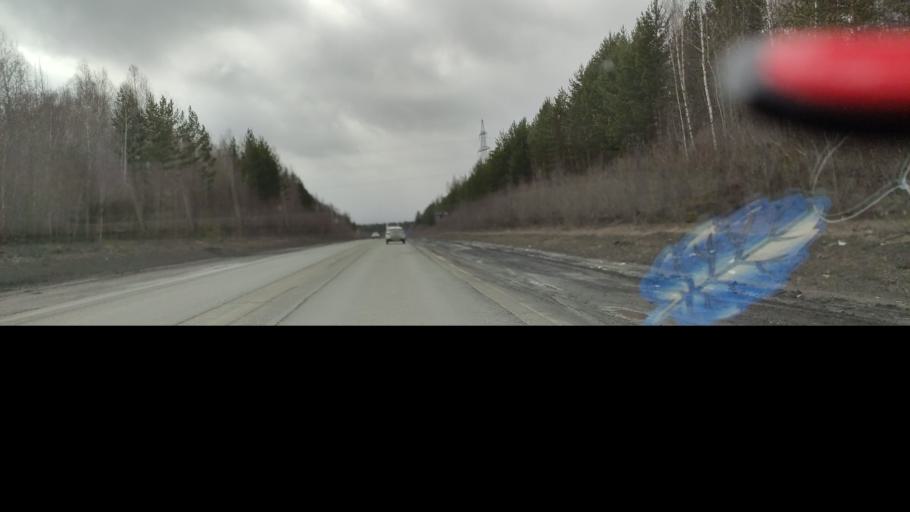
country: RU
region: Sverdlovsk
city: Talitsa
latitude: 56.8526
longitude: 60.0581
